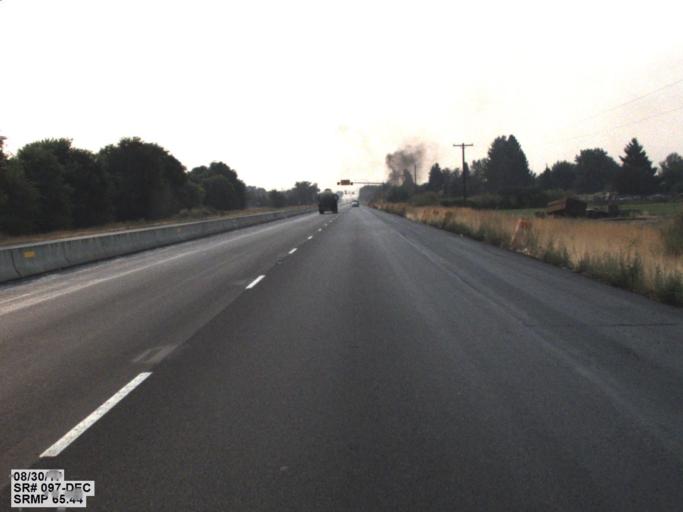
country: US
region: Washington
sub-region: Yakima County
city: Wapato
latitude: 46.4076
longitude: -120.3835
